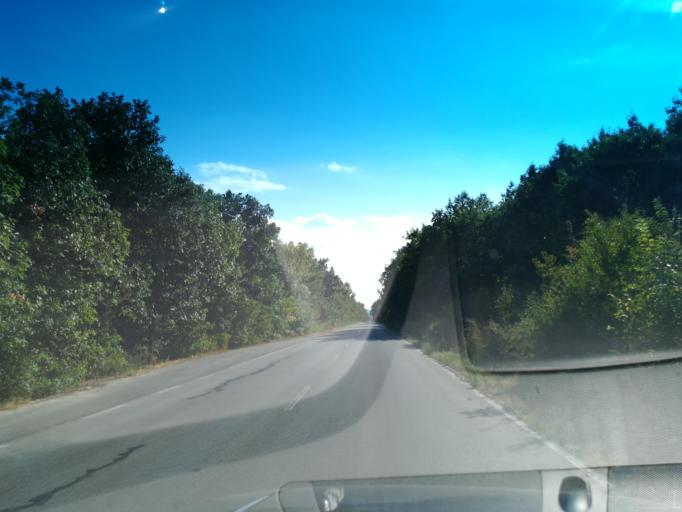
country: BG
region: Khaskovo
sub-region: Obshtina Mineralni Bani
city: Mineralni Bani
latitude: 41.9958
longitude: 25.3633
